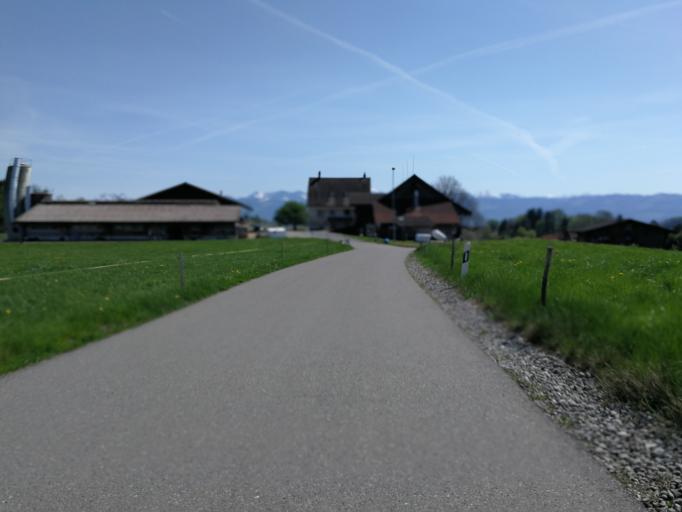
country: CH
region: Zurich
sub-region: Bezirk Hinwil
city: Durnten
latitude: 47.2842
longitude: 8.8245
